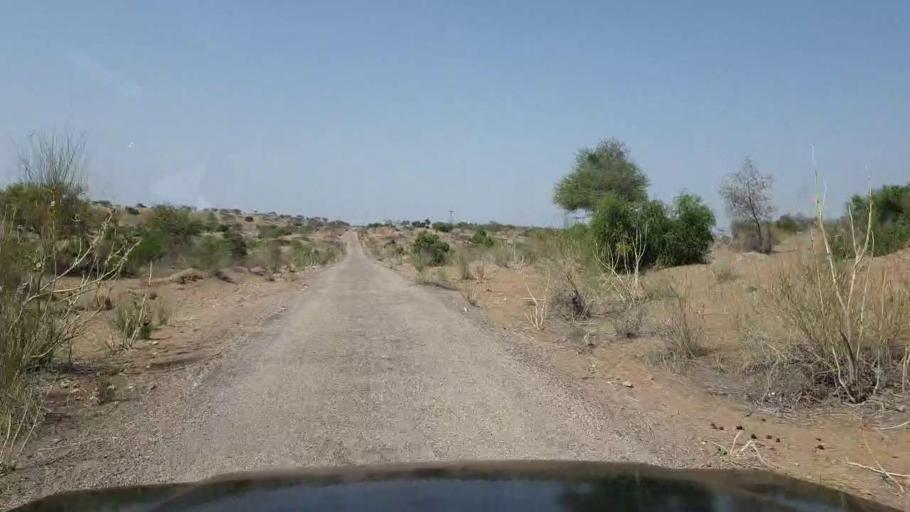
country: PK
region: Sindh
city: Mithi
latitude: 24.9754
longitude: 69.9720
